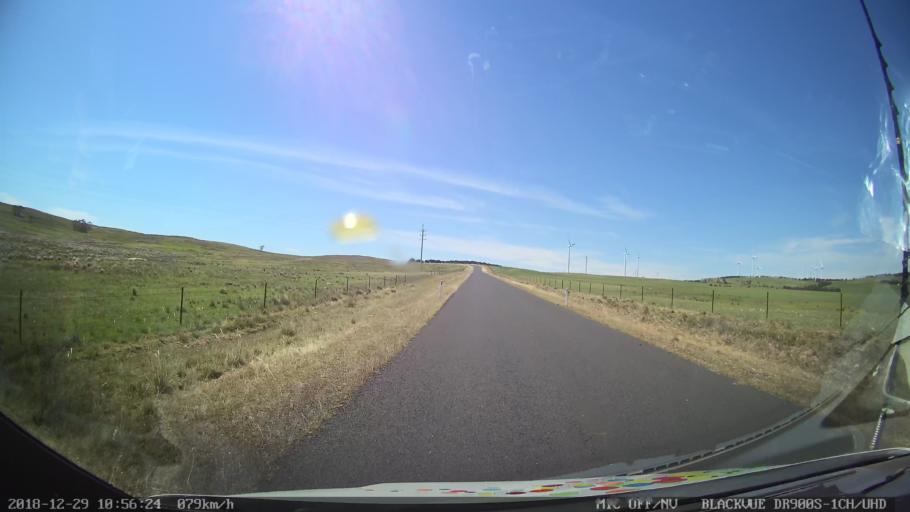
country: AU
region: New South Wales
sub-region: Palerang
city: Bungendore
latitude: -35.1338
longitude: 149.5382
